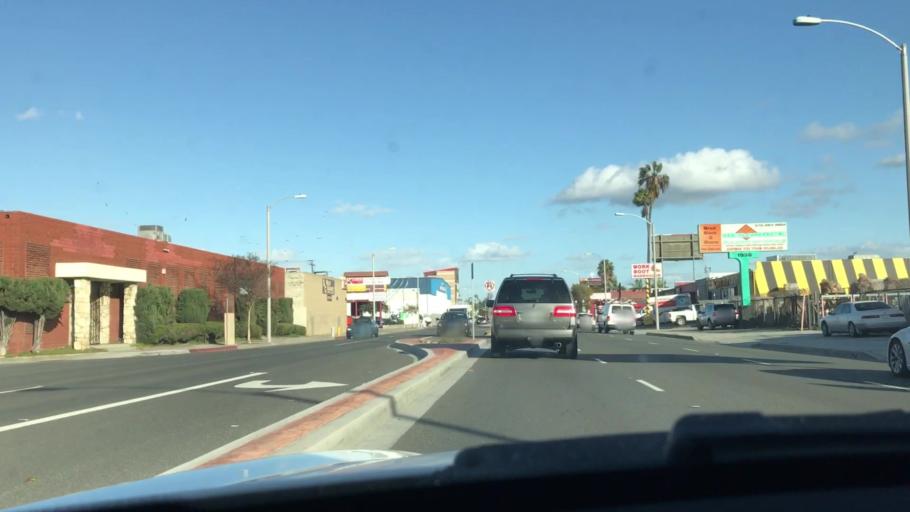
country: US
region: California
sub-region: Los Angeles County
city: Gardena
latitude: 33.9019
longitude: -118.3045
